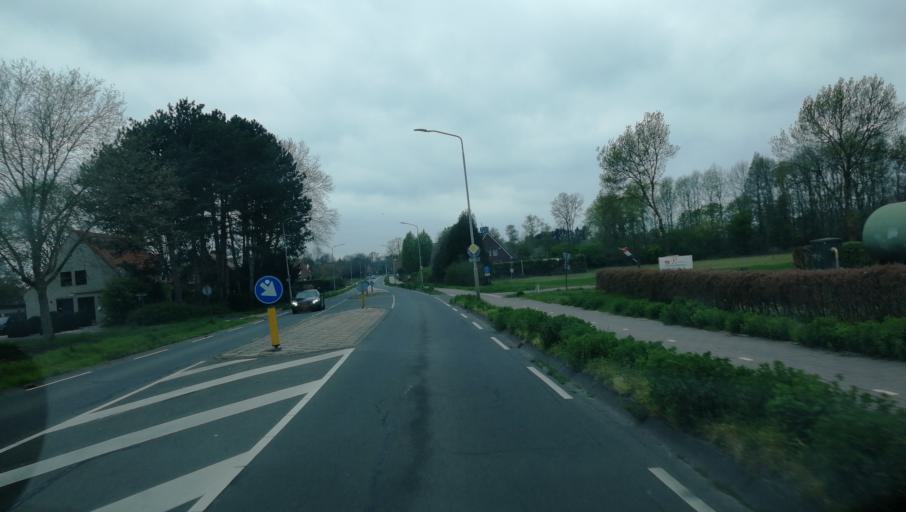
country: NL
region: Limburg
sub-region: Gemeente Venlo
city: Venlo
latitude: 51.3762
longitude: 6.1993
